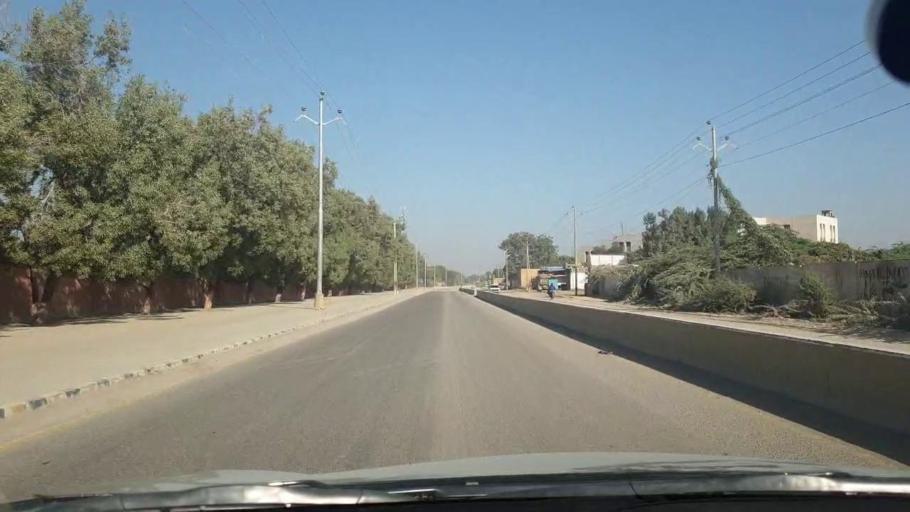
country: PK
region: Sindh
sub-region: Karachi District
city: Karachi
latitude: 25.0813
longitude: 67.0130
